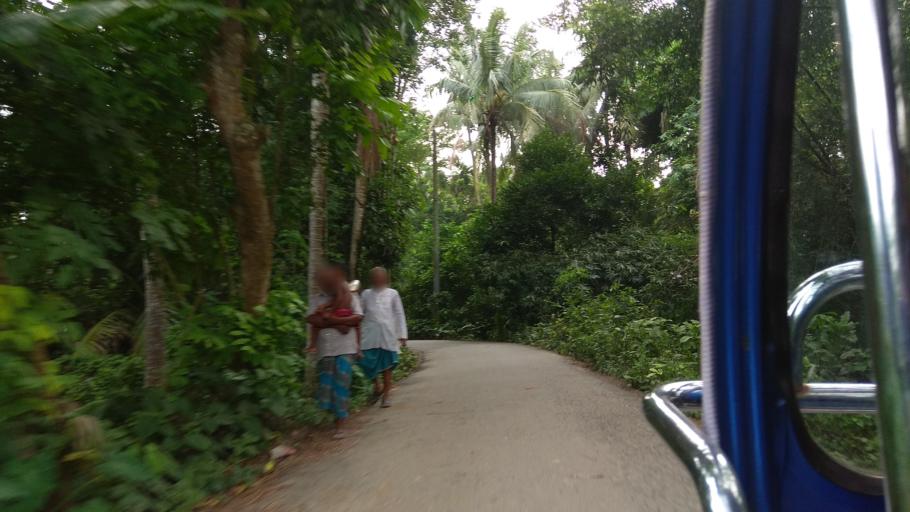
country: BD
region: Khulna
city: Kalia
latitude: 23.0309
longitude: 89.6537
